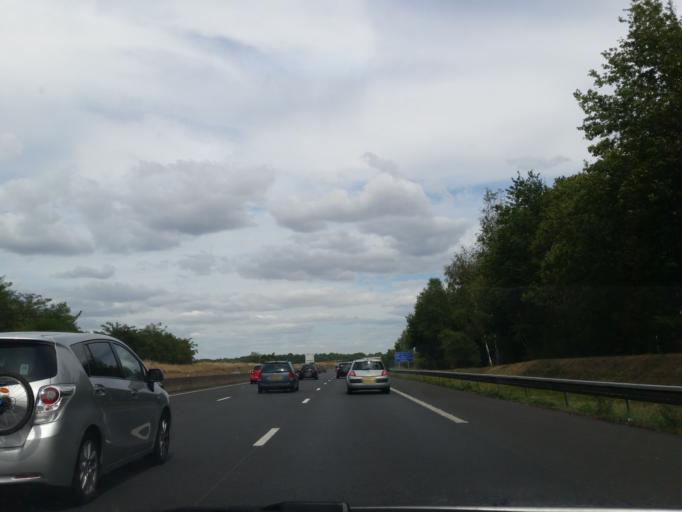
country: FR
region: Centre
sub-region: Departement d'Indre-et-Loire
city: Monnaie
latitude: 47.4821
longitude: 0.7925
